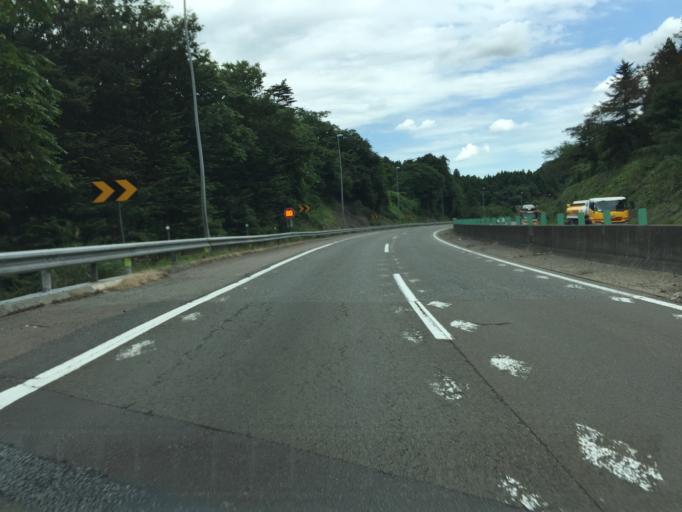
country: JP
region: Miyagi
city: Sendai
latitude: 38.2009
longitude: 140.7870
